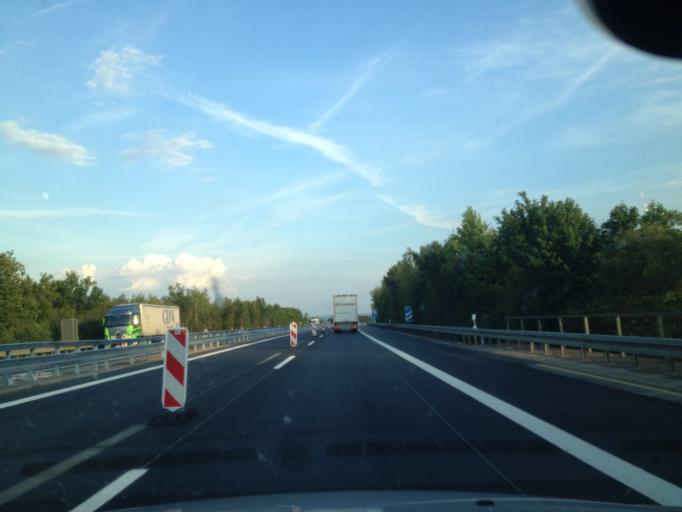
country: DE
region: Bavaria
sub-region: Regierungsbezirk Unterfranken
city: Biebelried
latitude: 49.7642
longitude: 10.1033
